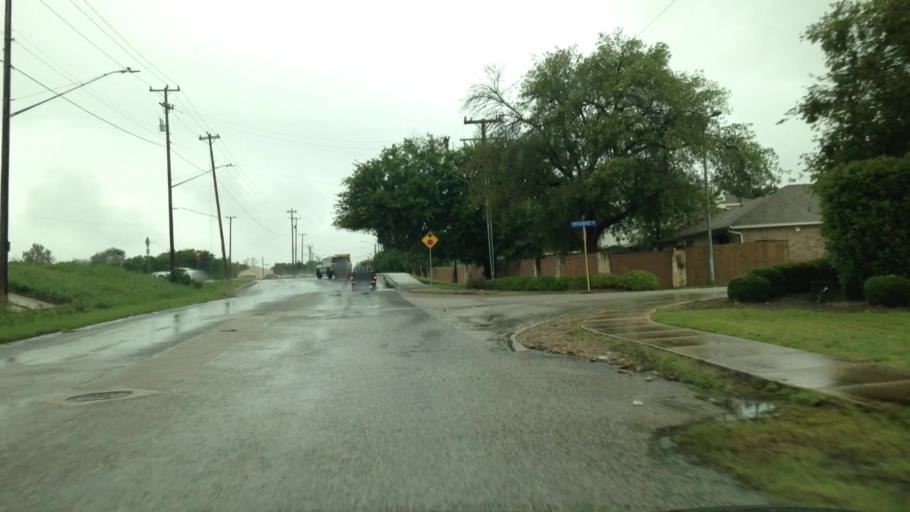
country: US
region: Texas
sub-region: Bexar County
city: Live Oak
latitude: 29.5684
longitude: -98.3661
